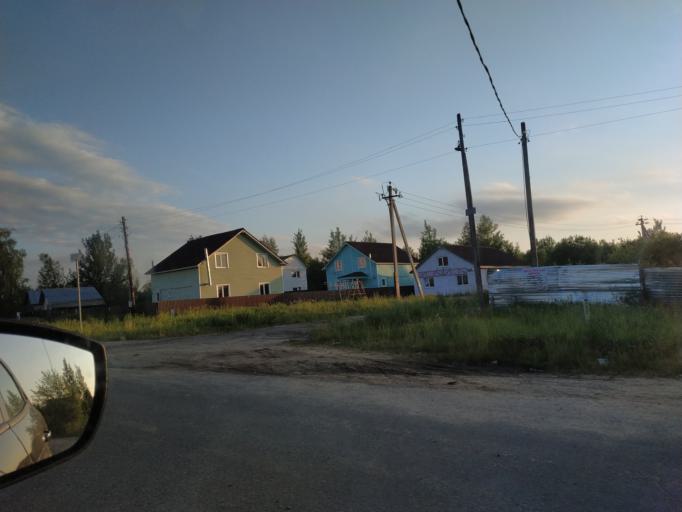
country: RU
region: Moskovskaya
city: Krasnoarmeysk
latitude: 56.0858
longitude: 38.2252
